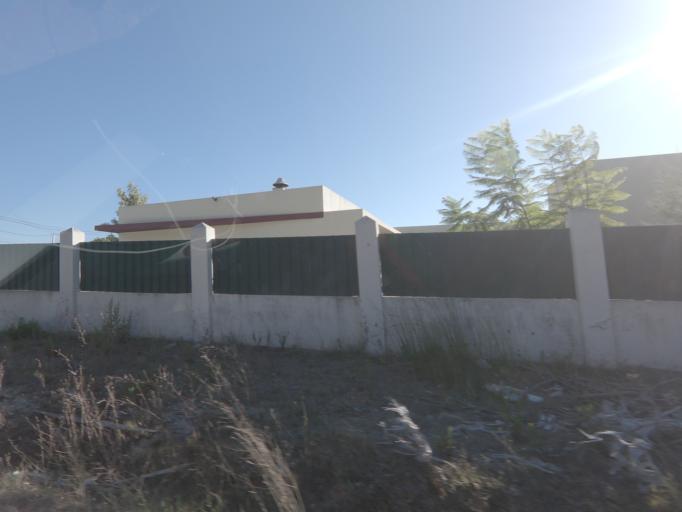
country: PT
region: Setubal
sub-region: Moita
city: Moita
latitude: 38.6278
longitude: -8.9629
